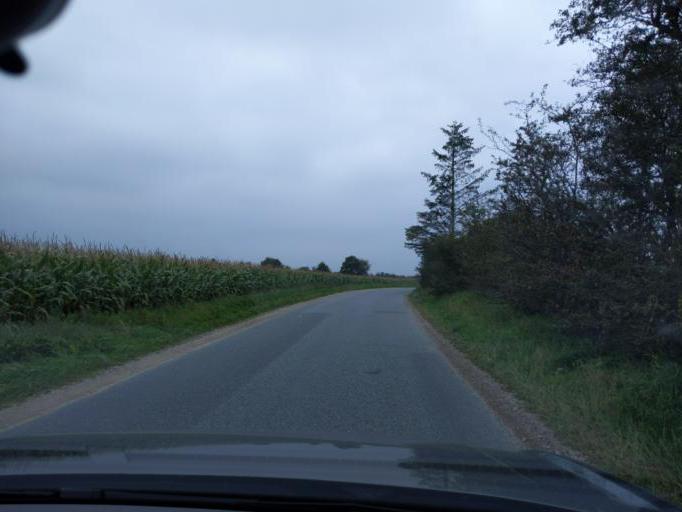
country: DK
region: Central Jutland
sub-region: Viborg Kommune
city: Stoholm
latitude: 56.5088
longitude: 9.2536
